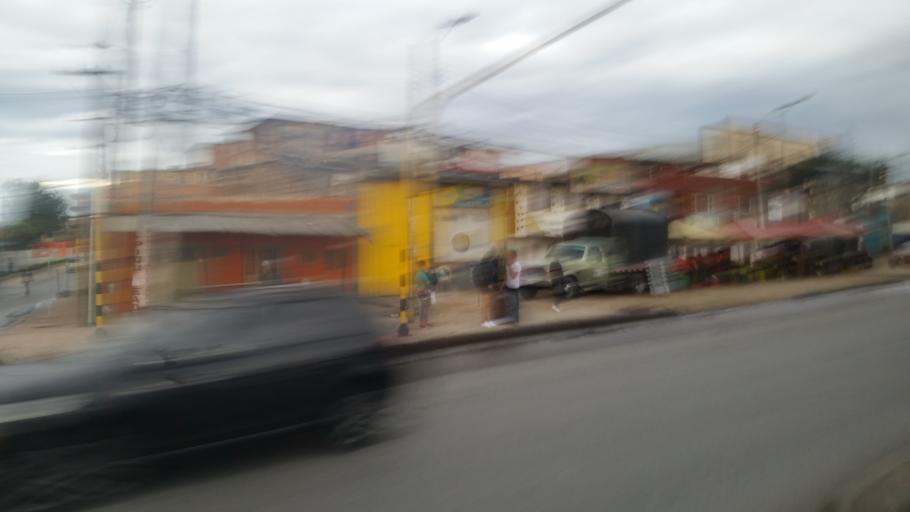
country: CO
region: Cundinamarca
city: Funza
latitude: 4.6942
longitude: -74.1688
